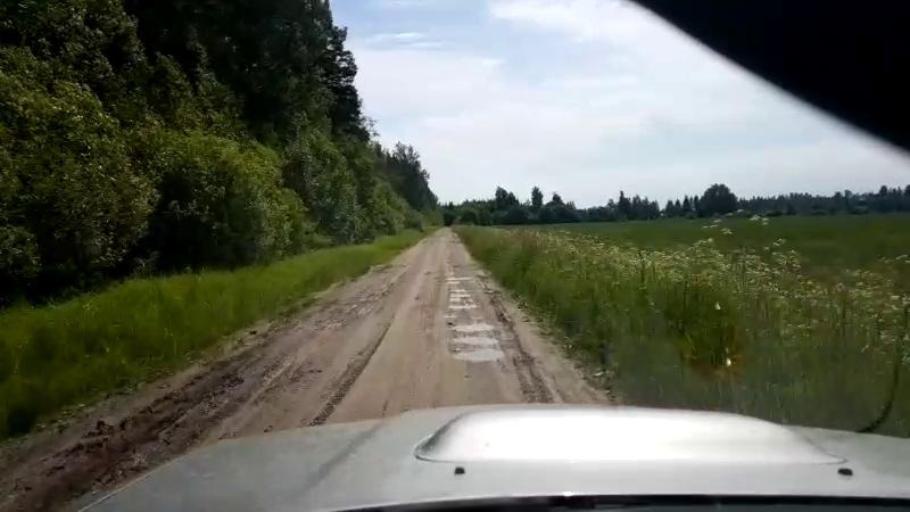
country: EE
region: Paernumaa
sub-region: Sindi linn
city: Sindi
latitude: 58.5311
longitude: 24.6683
